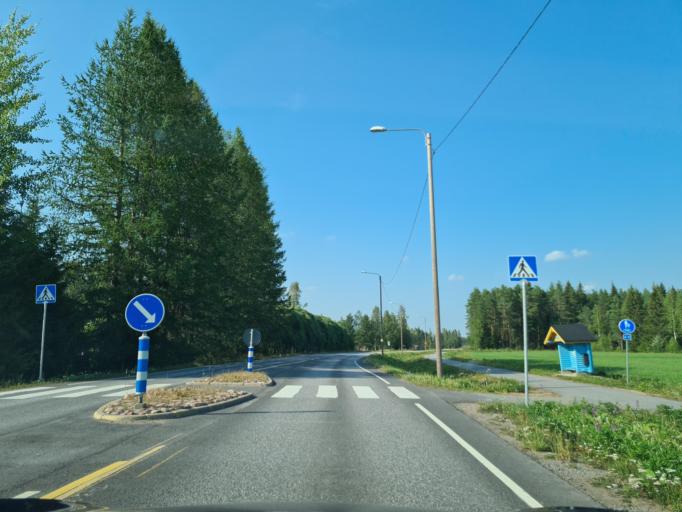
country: FI
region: Satakunta
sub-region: Pohjois-Satakunta
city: Karvia
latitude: 62.0884
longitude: 22.5270
